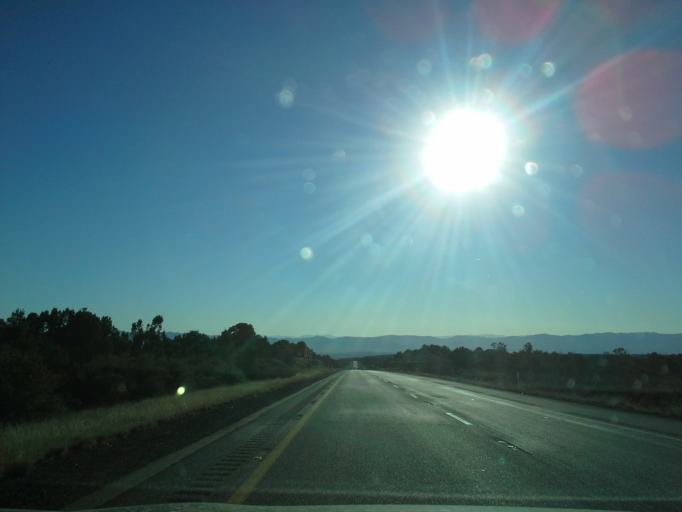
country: US
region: Arizona
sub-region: Yavapai County
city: Village of Oak Creek (Big Park)
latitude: 34.7442
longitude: -111.6860
